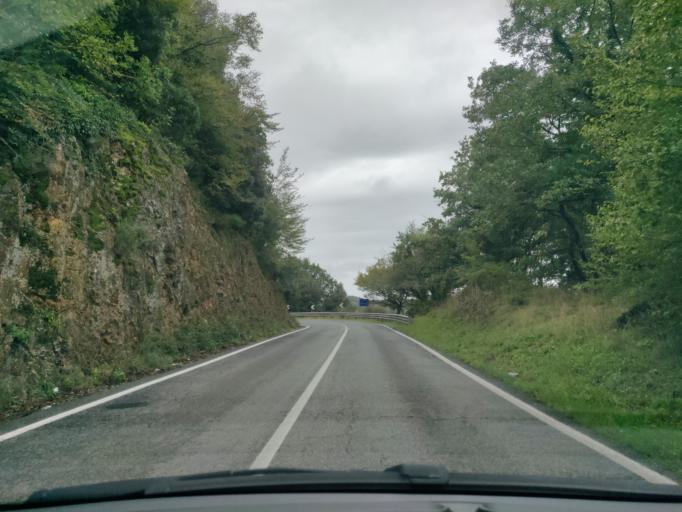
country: IT
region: Latium
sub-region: Citta metropolitana di Roma Capitale
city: Allumiere
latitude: 42.1521
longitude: 11.8991
